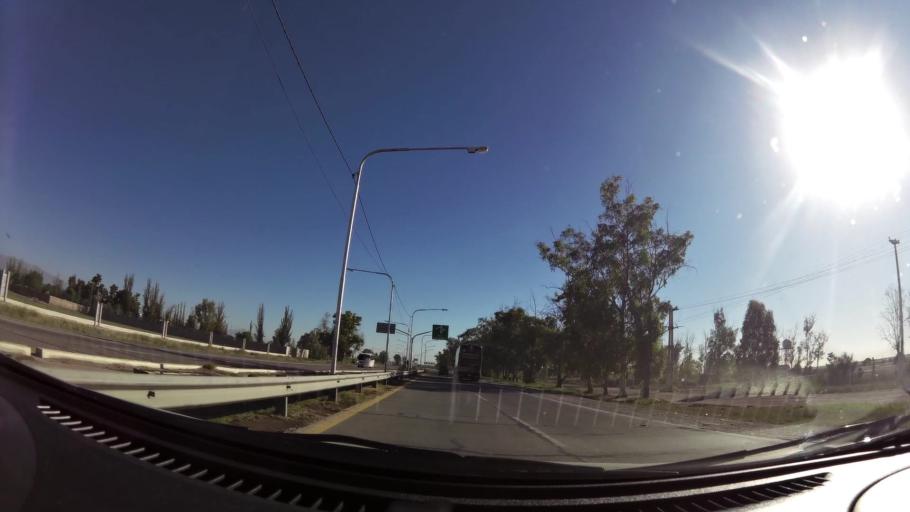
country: AR
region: Mendoza
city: Las Heras
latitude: -32.8258
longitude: -68.8038
